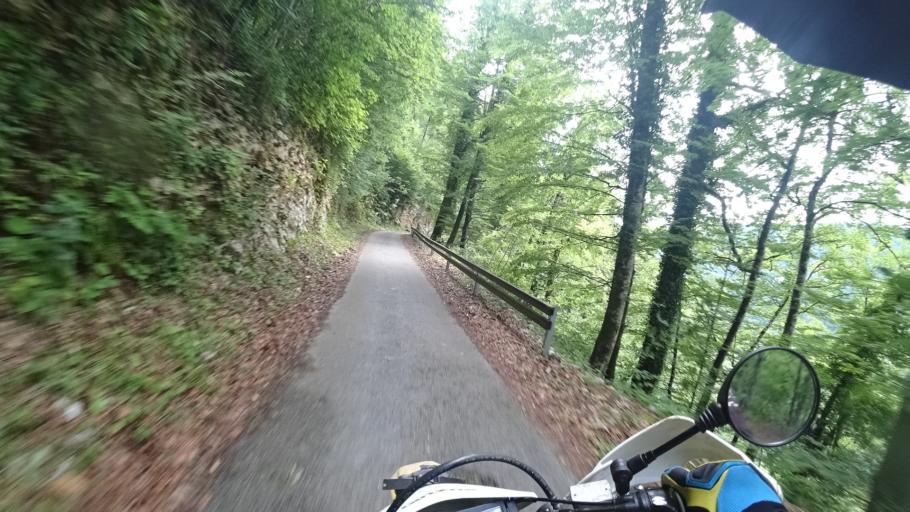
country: SI
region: Osilnica
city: Osilnica
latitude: 45.4976
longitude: 14.7034
